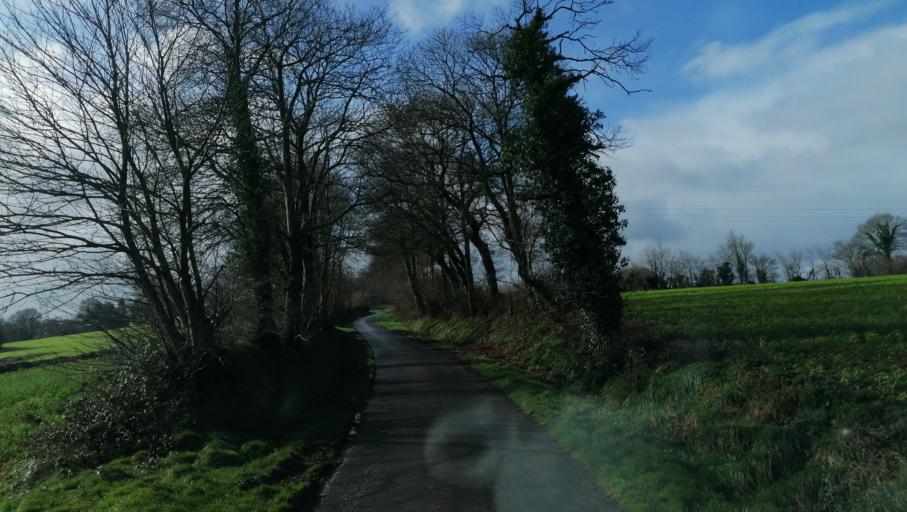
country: FR
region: Brittany
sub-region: Departement des Cotes-d'Armor
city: Lanrodec
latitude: 48.4934
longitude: -3.0191
